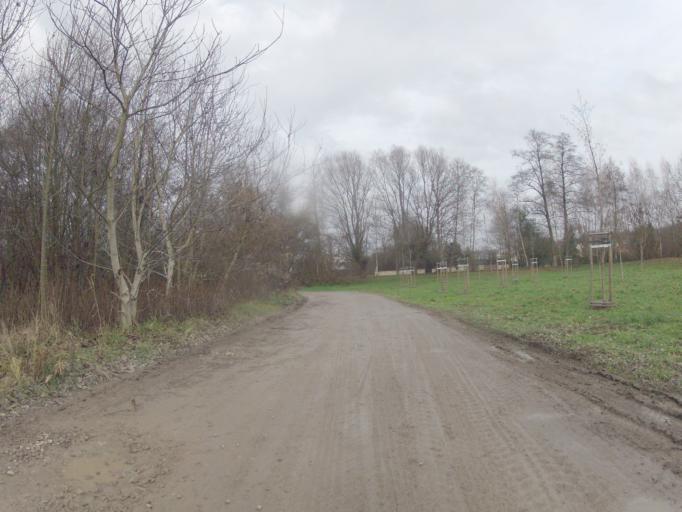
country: PL
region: Lesser Poland Voivodeship
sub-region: Powiat krakowski
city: Rzaska
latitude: 50.0788
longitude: 19.8568
